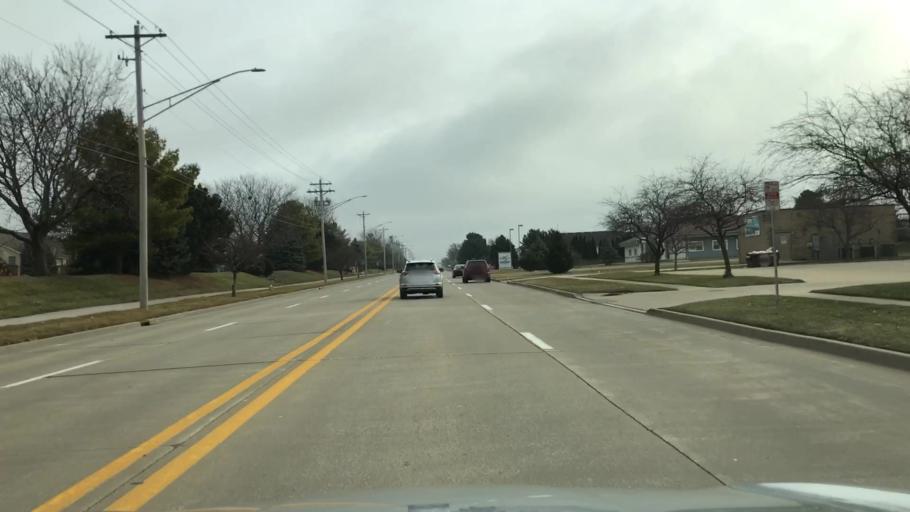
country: US
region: Illinois
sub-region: McLean County
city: Normal
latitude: 40.5026
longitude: -88.9115
